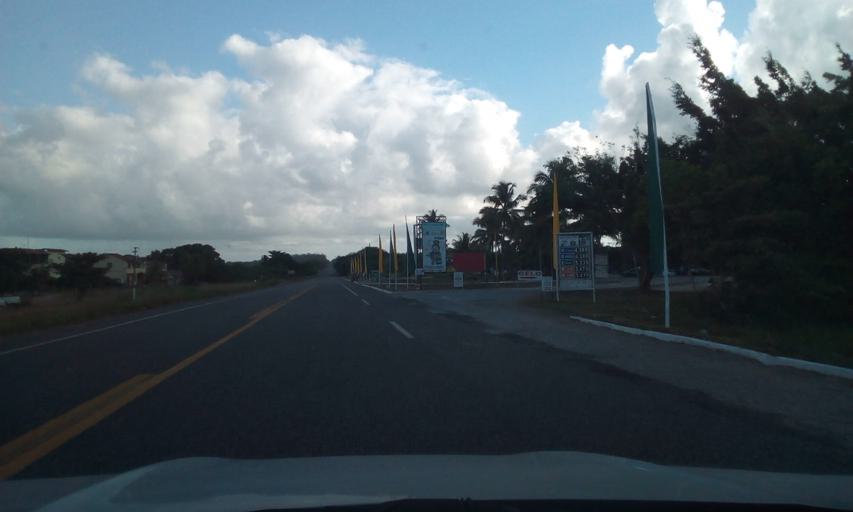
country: BR
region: Bahia
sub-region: Entre Rios
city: Entre Rios
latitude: -12.3028
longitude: -37.9009
